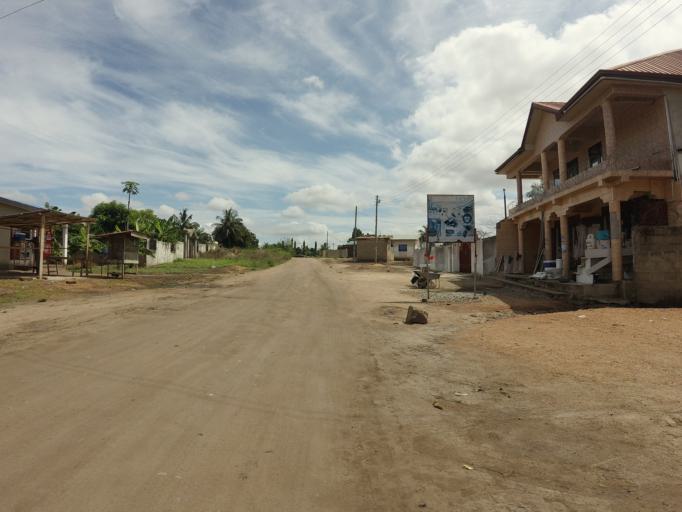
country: GH
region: Central
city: Kasoa
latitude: 5.5209
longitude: -0.4523
